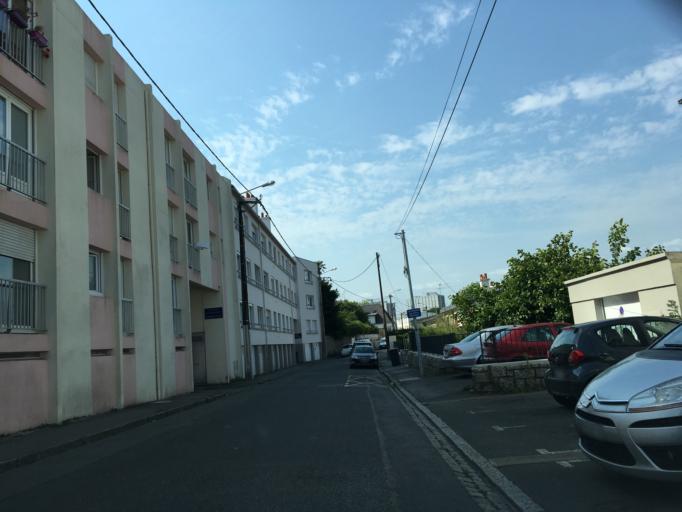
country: FR
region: Brittany
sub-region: Departement du Morbihan
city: Lorient
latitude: 47.7600
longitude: -3.3694
